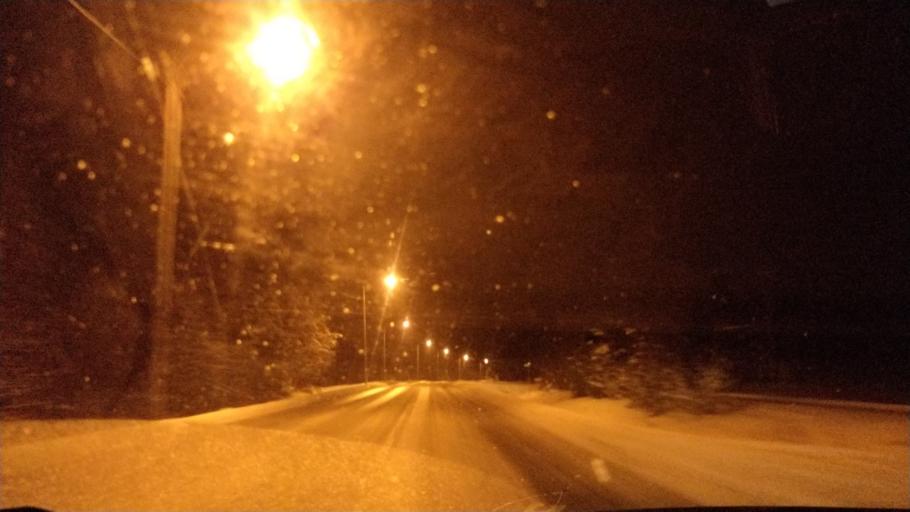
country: FI
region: Lapland
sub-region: Rovaniemi
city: Rovaniemi
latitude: 66.3127
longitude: 25.3617
